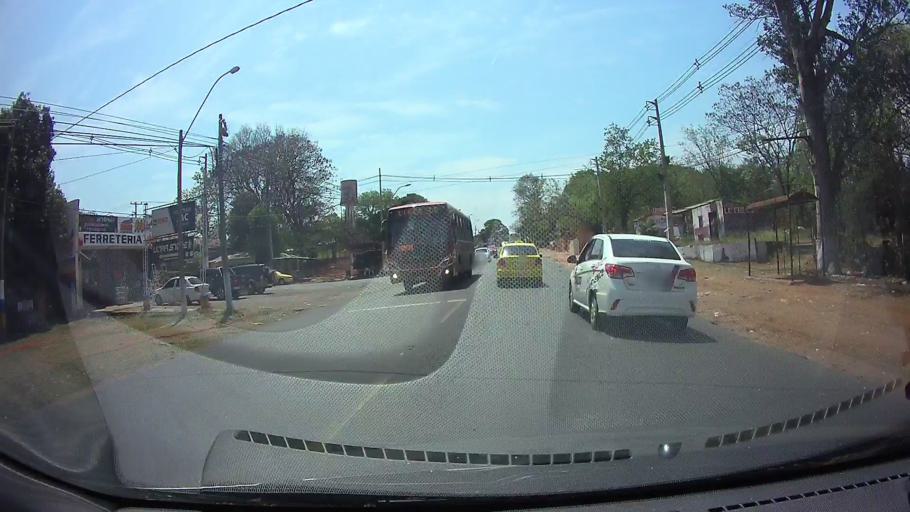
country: PY
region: Central
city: Capiata
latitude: -25.3870
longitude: -57.4713
